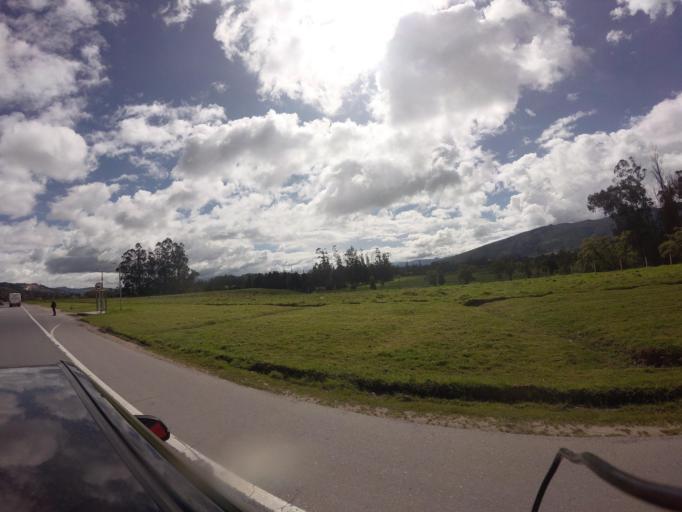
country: CO
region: Cundinamarca
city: Gachancipa
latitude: 4.9905
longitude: -73.8792
